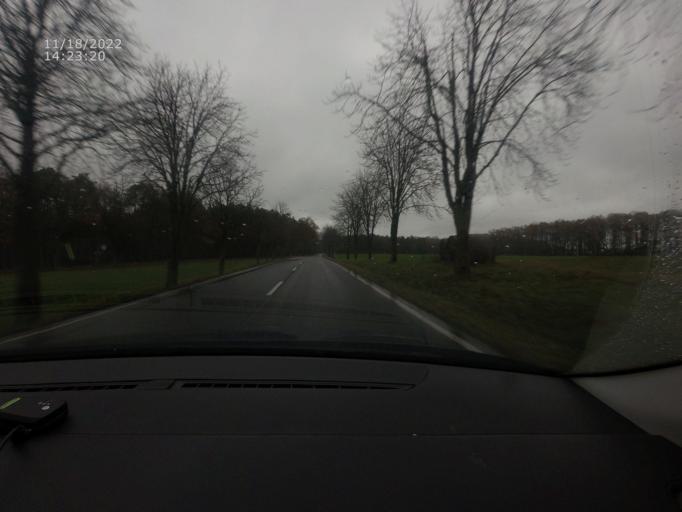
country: CZ
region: Jihocesky
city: Cimelice
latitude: 49.4397
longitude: 14.1072
